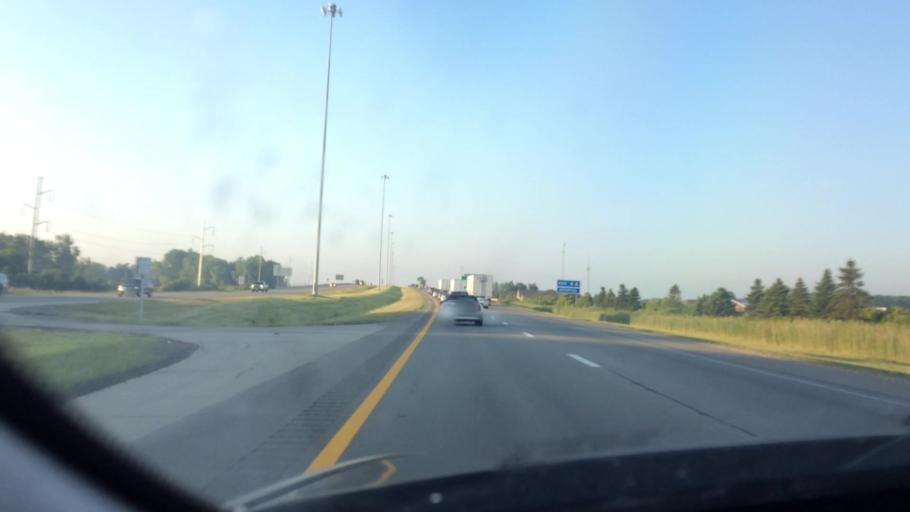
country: US
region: Ohio
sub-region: Lucas County
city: Maumee
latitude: 41.5656
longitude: -83.6904
